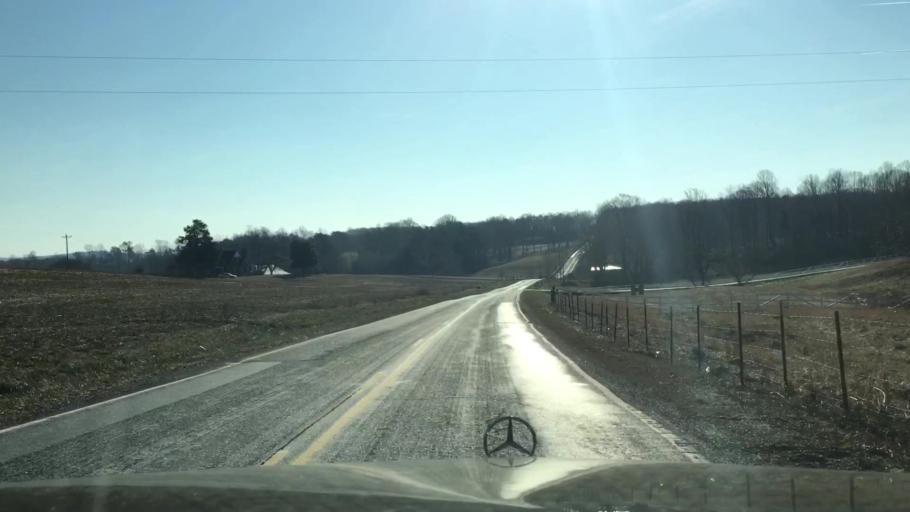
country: US
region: Virginia
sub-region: Pittsylvania County
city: Motley
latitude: 37.1905
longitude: -79.4237
